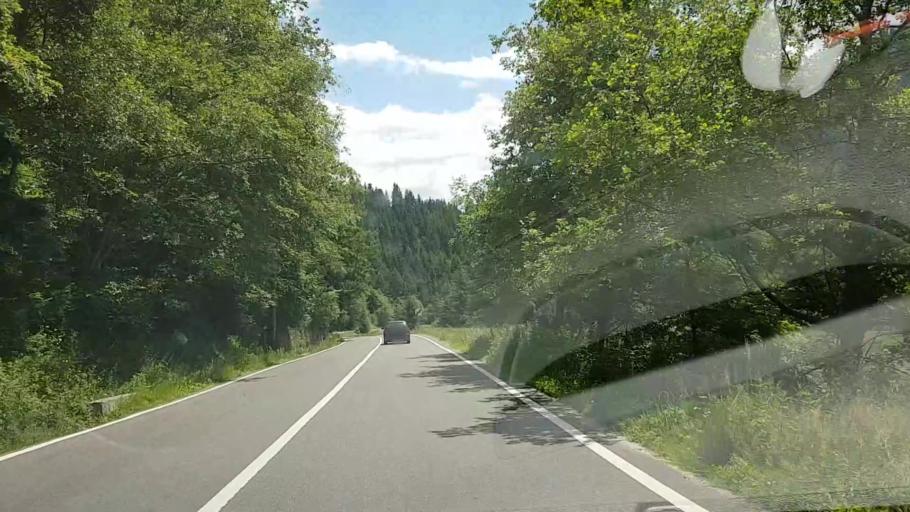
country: RO
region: Suceava
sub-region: Comuna Brosteni
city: Brosteni
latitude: 47.2634
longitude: 25.6651
